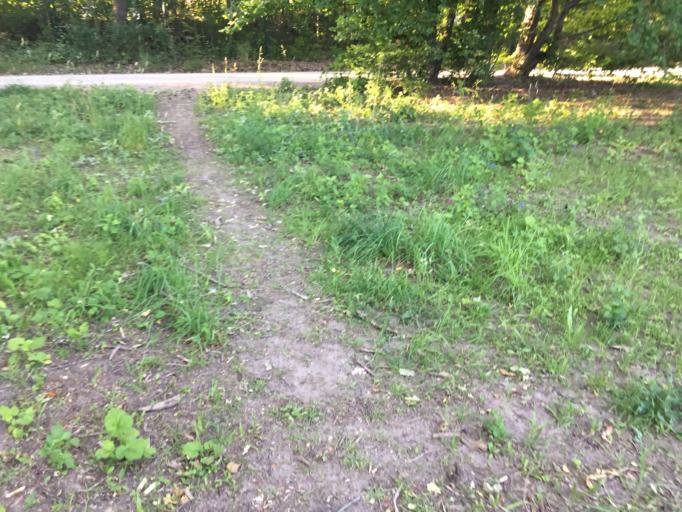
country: DE
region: Bavaria
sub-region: Regierungsbezirk Mittelfranken
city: Erlangen
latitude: 49.5698
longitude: 11.0095
